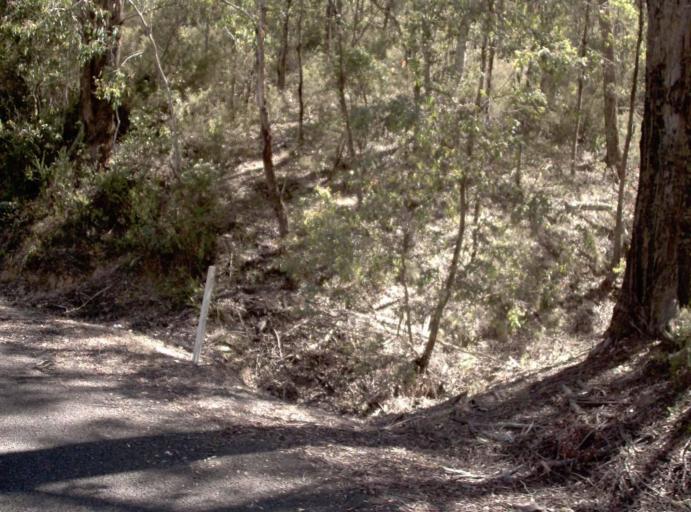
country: AU
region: New South Wales
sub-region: Bombala
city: Bombala
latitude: -37.1469
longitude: 148.7241
